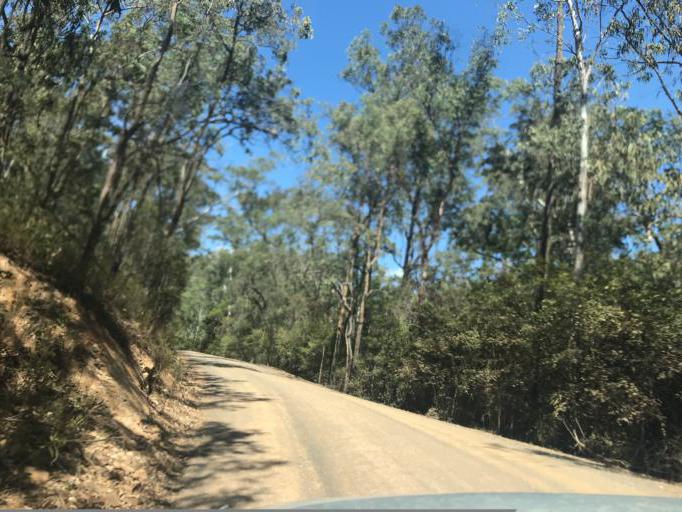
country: AU
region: New South Wales
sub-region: Wyong Shire
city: Little Jilliby
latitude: -33.1822
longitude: 151.0545
